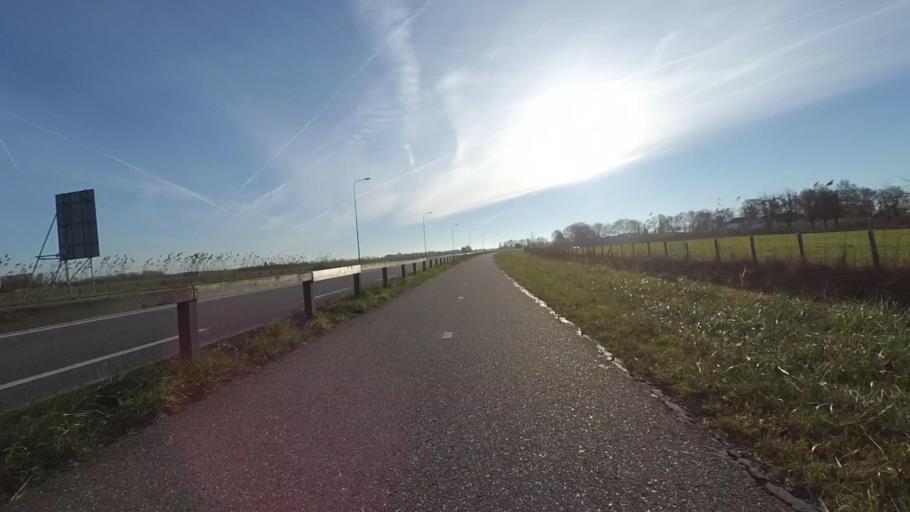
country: NL
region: Utrecht
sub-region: Gemeente Wijk bij Duurstede
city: Wijk bij Duurstede
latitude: 51.9966
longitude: 5.3219
